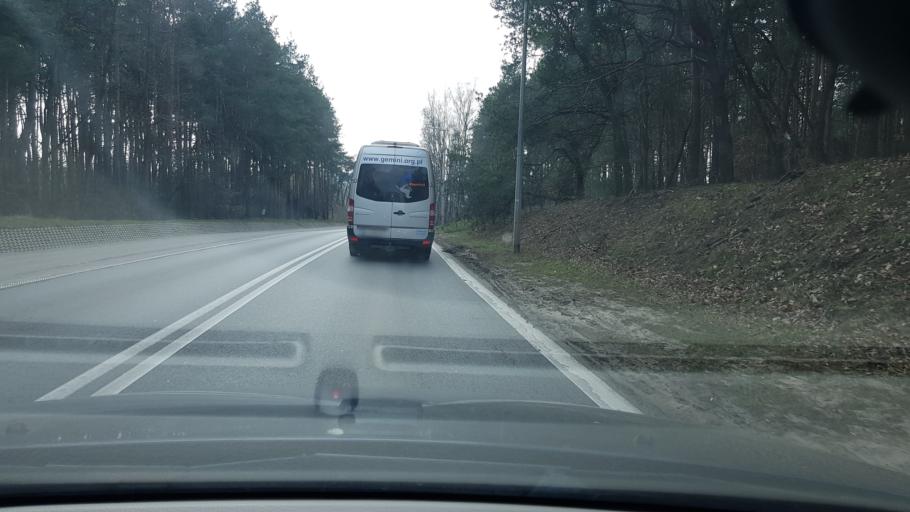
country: PL
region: Masovian Voivodeship
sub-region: Warszawa
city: Wesola
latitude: 52.2265
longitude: 21.2238
